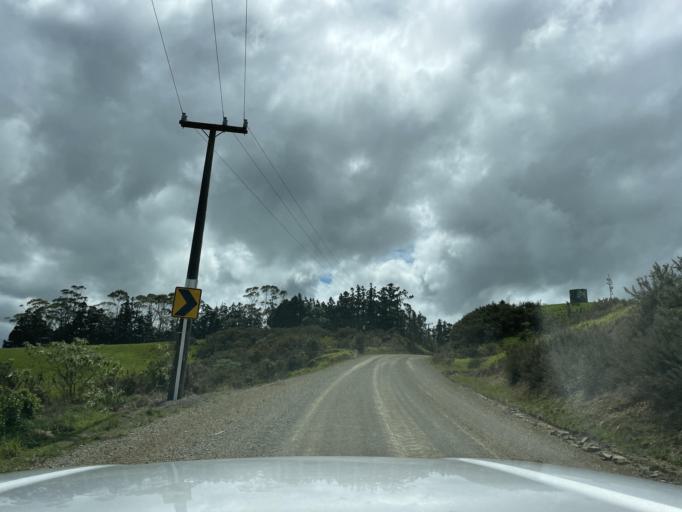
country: NZ
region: Auckland
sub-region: Auckland
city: Wellsford
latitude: -36.1458
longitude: 174.5414
